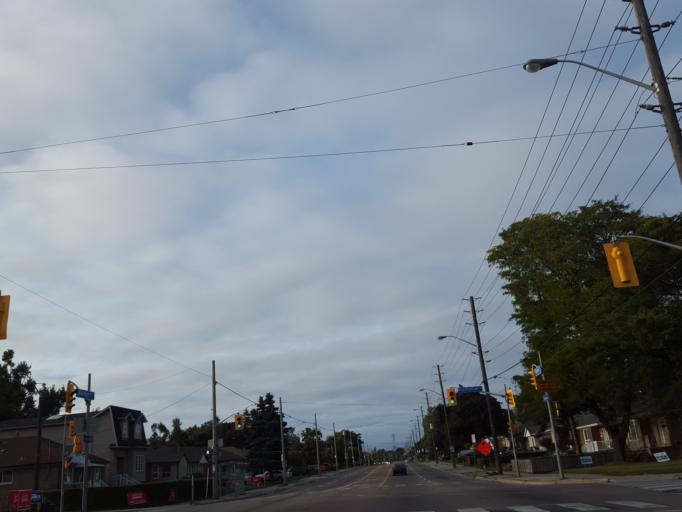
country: CA
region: Ontario
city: Scarborough
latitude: 43.7516
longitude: -79.2972
